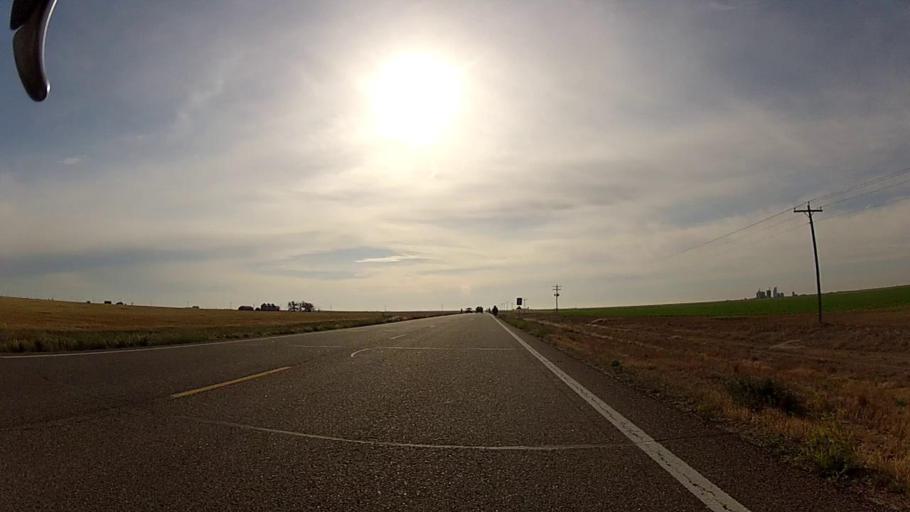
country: US
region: Kansas
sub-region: Grant County
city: Ulysses
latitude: 37.5765
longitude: -101.4781
